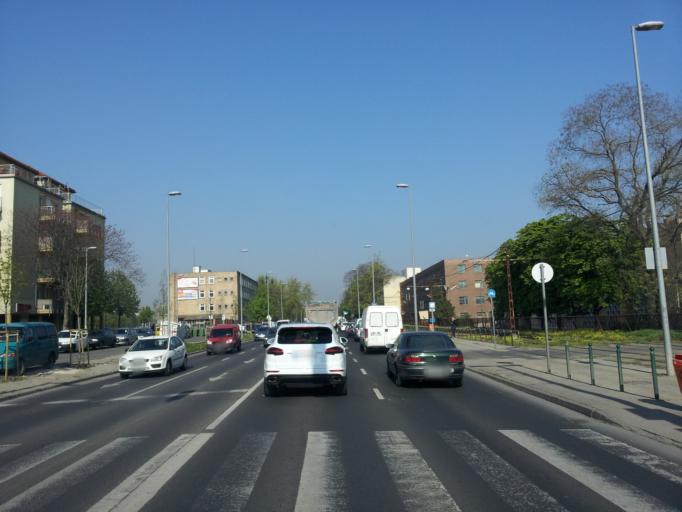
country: HU
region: Budapest
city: Budapest XIV. keruelet
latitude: 47.4849
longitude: 19.1138
